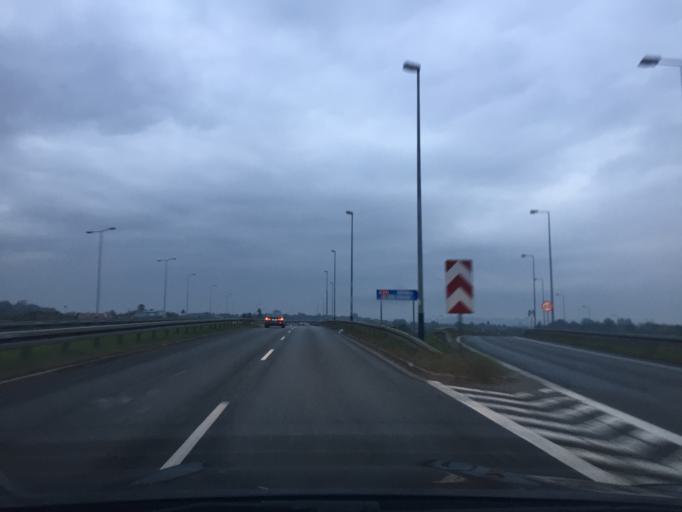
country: PL
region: Lesser Poland Voivodeship
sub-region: Powiat krakowski
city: Wrzasowice
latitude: 50.0029
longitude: 19.9415
